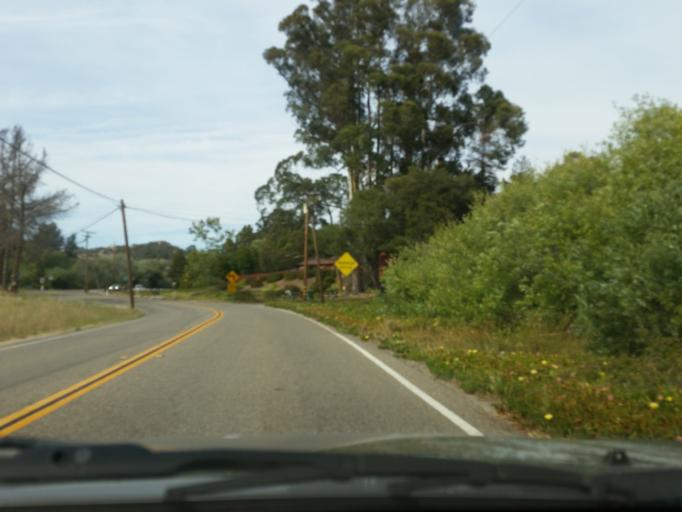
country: US
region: California
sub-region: San Luis Obispo County
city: Arroyo Grande
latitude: 35.1327
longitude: -120.5701
